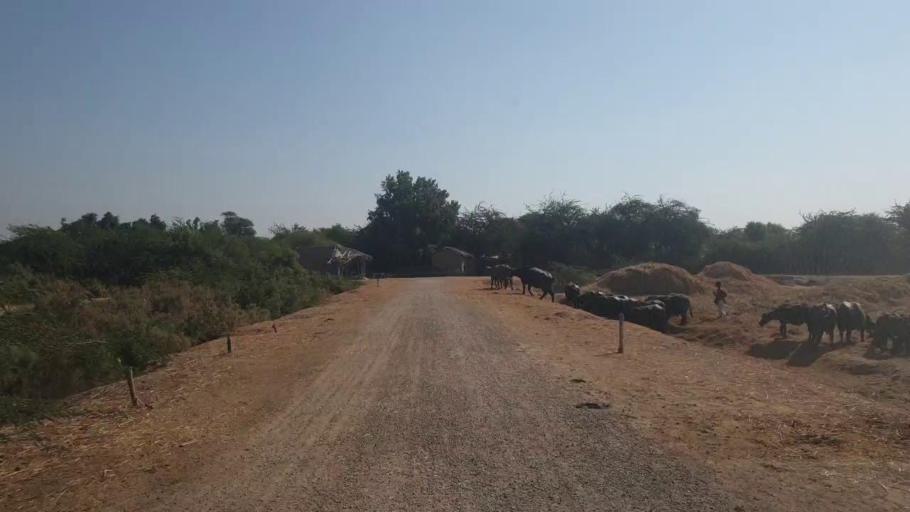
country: PK
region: Sindh
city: Badin
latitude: 24.5517
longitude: 68.8474
